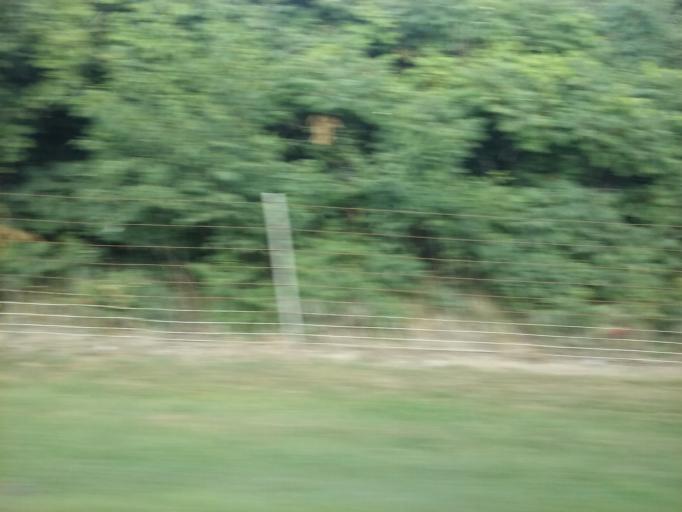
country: US
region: Ohio
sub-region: Wood County
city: Bowling Green
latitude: 41.3152
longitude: -83.6503
